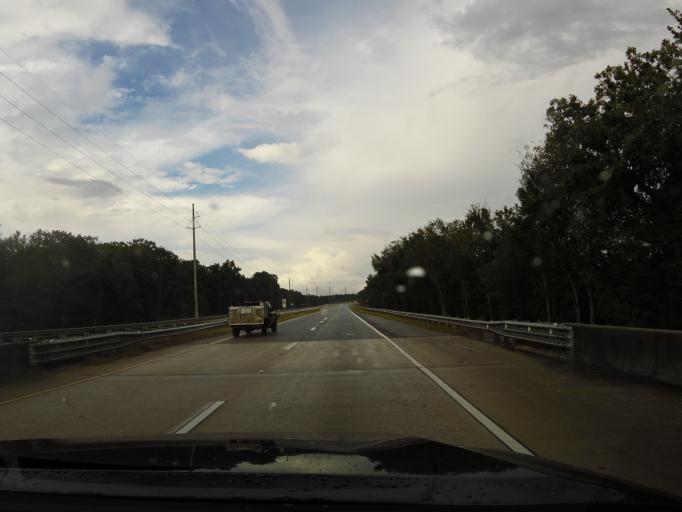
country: US
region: Georgia
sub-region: Long County
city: Ludowici
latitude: 31.6748
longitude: -81.8238
